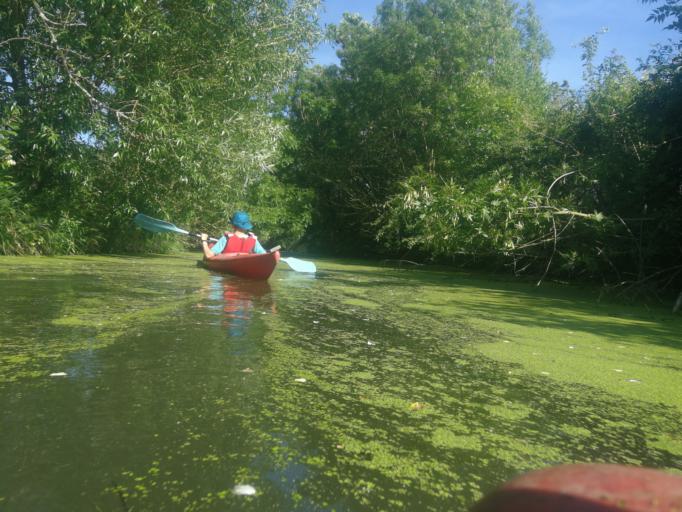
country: FR
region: Poitou-Charentes
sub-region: Departement de la Charente-Maritime
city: Marans
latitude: 46.3619
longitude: -0.9563
